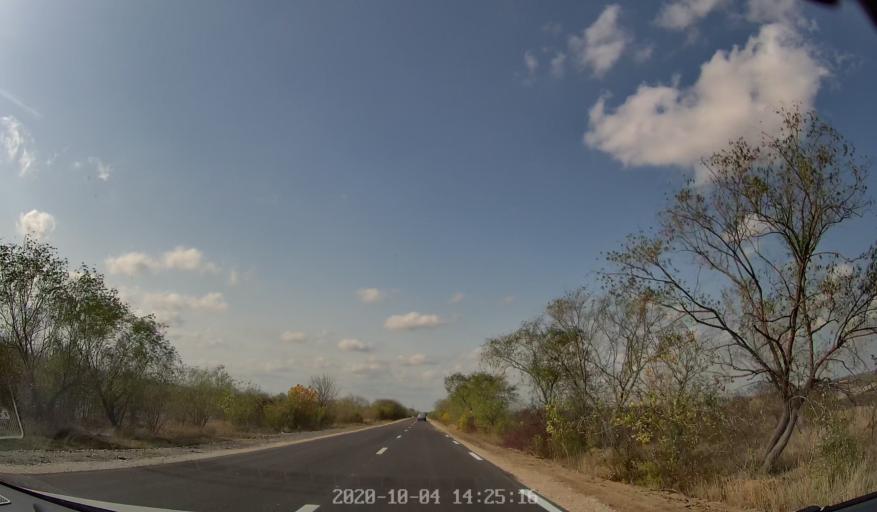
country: MD
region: Rezina
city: Saharna
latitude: 47.6192
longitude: 28.9017
